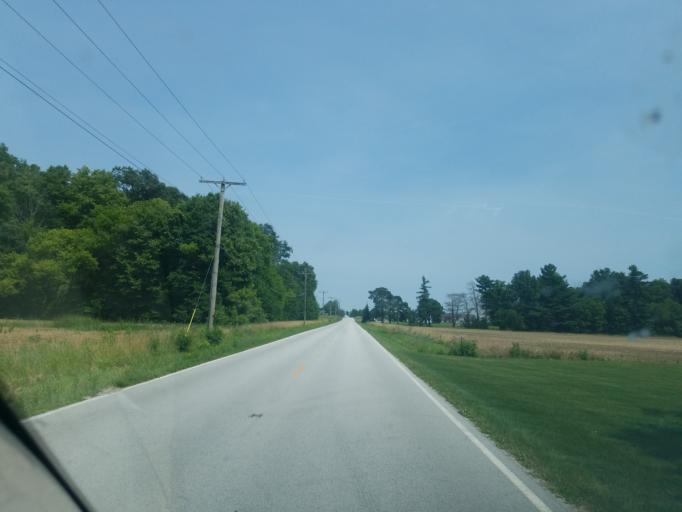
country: US
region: Ohio
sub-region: Wyandot County
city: Carey
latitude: 41.0507
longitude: -83.3335
